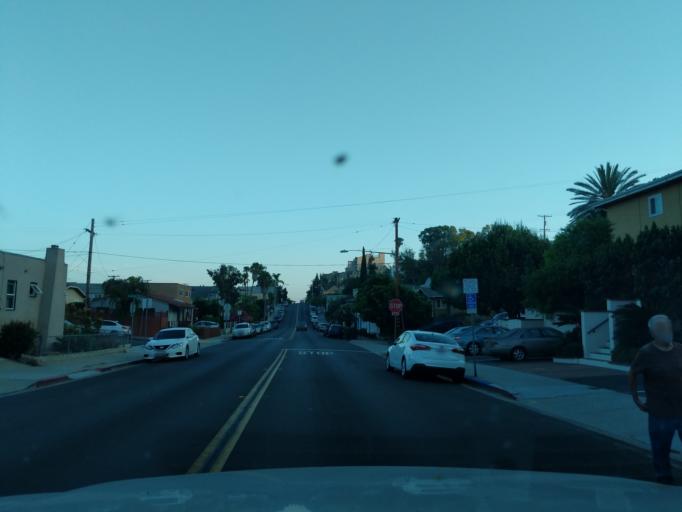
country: US
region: California
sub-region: San Diego County
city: San Diego
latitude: 32.7507
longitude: -117.1438
